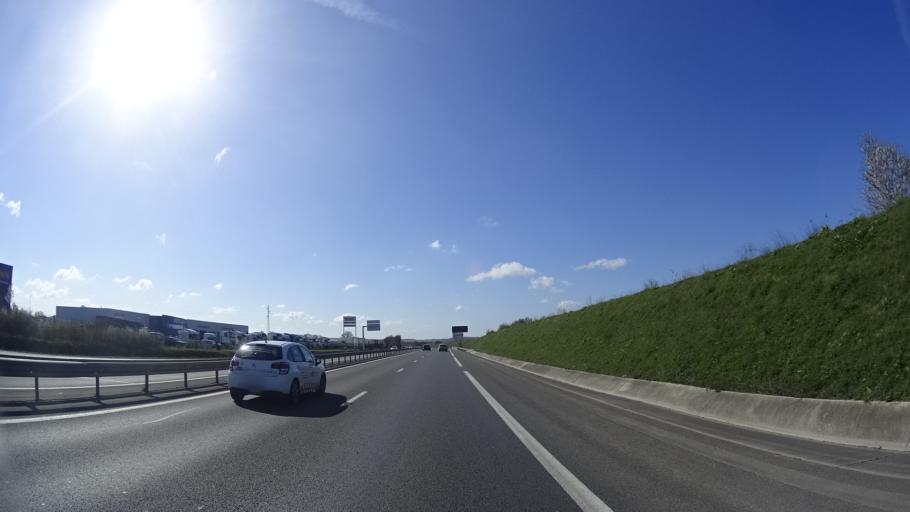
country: FR
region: Pays de la Loire
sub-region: Departement de Maine-et-Loire
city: Avrille
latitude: 47.5117
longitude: -0.6183
